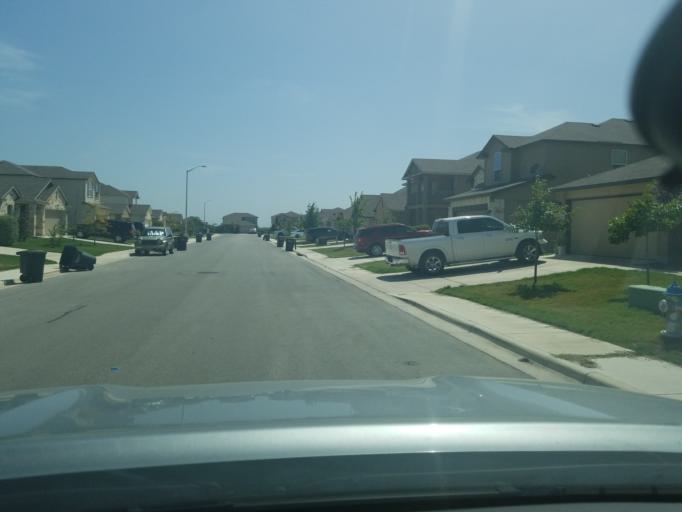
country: US
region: Texas
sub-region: Guadalupe County
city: Lake Dunlap
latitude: 29.6694
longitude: -98.0384
